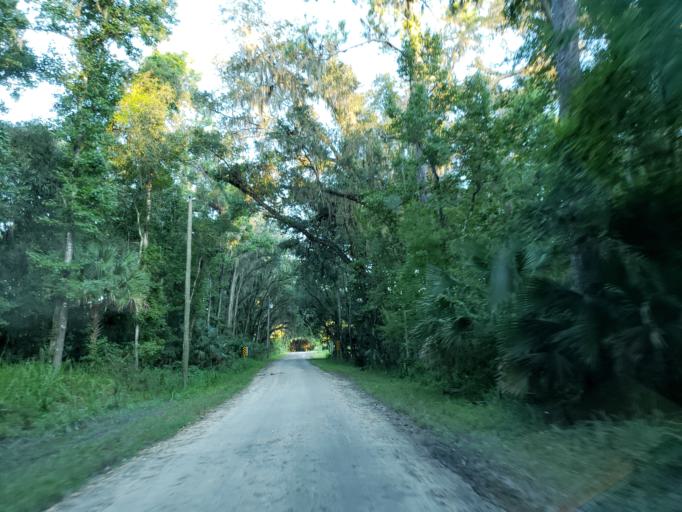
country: US
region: Florida
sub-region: Alachua County
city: Gainesville
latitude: 29.4924
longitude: -82.2813
